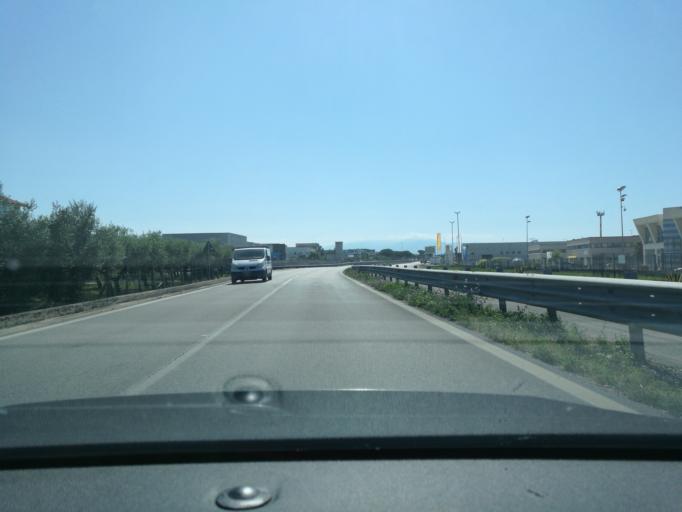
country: IT
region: Abruzzo
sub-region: Provincia di Chieti
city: Vasto
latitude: 42.1672
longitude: 14.6928
